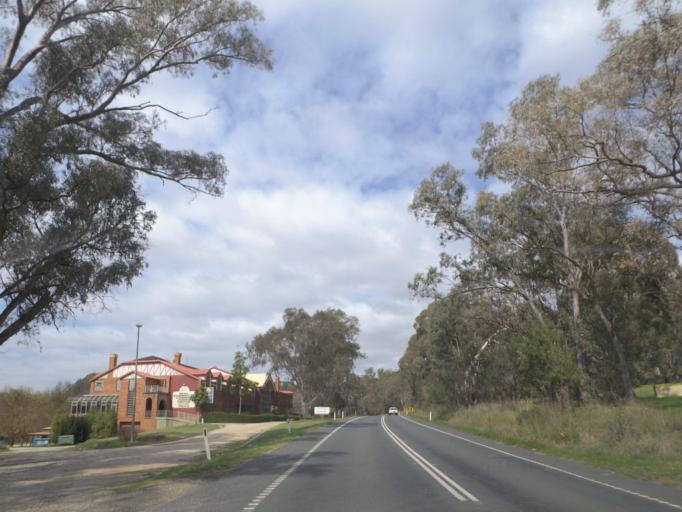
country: AU
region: Victoria
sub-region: Murrindindi
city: Kinglake West
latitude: -37.1189
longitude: 145.2147
